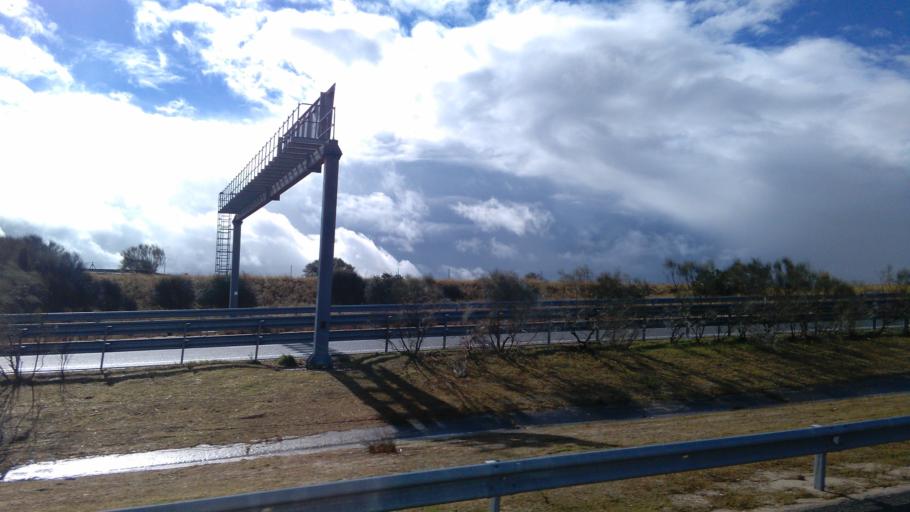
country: ES
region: Madrid
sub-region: Provincia de Madrid
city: Navalcarnero
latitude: 40.2658
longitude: -4.0175
